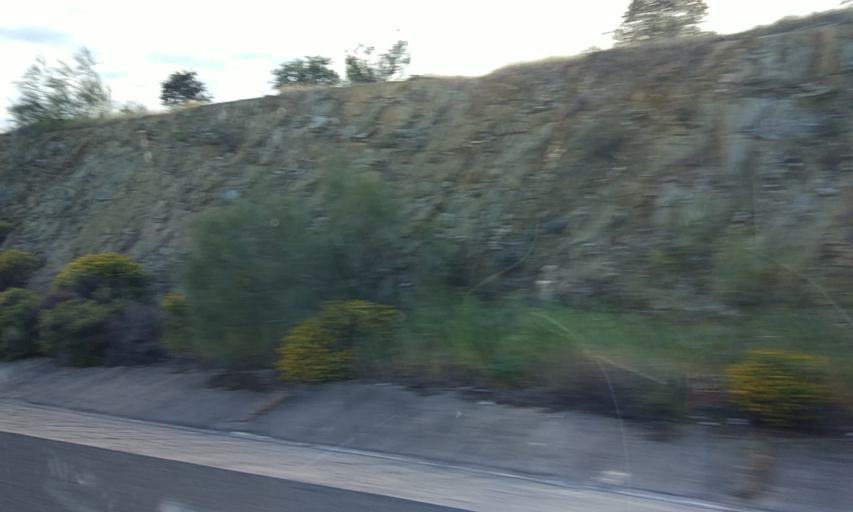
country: ES
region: Extremadura
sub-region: Provincia de Caceres
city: Canaveral
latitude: 39.7456
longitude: -6.4042
